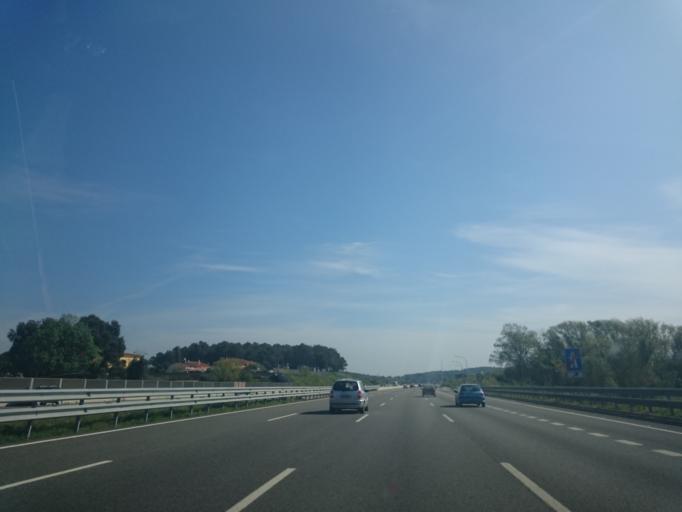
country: ES
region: Catalonia
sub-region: Provincia de Girona
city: Salt
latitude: 41.9908
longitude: 2.7895
